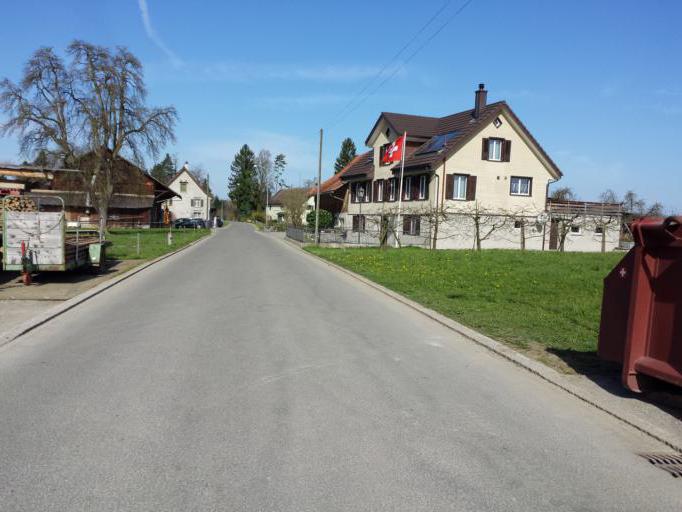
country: CH
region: Thurgau
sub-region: Arbon District
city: Salmsach
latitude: 47.5439
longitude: 9.3520
